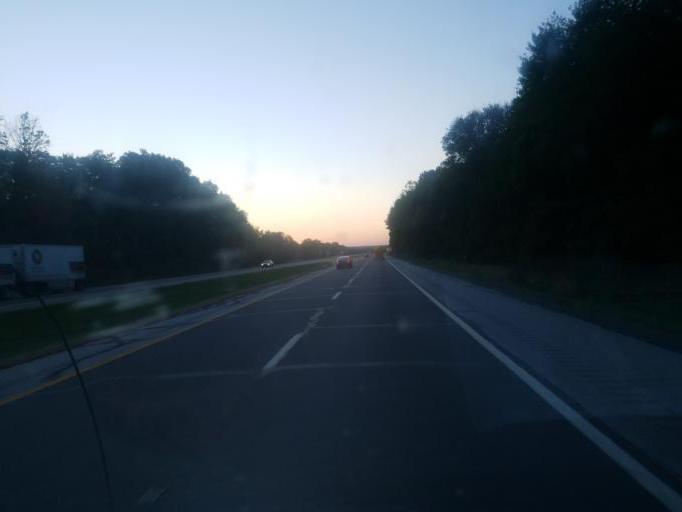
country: US
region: Ohio
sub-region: Mahoning County
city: Canfield
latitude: 41.0229
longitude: -80.7207
